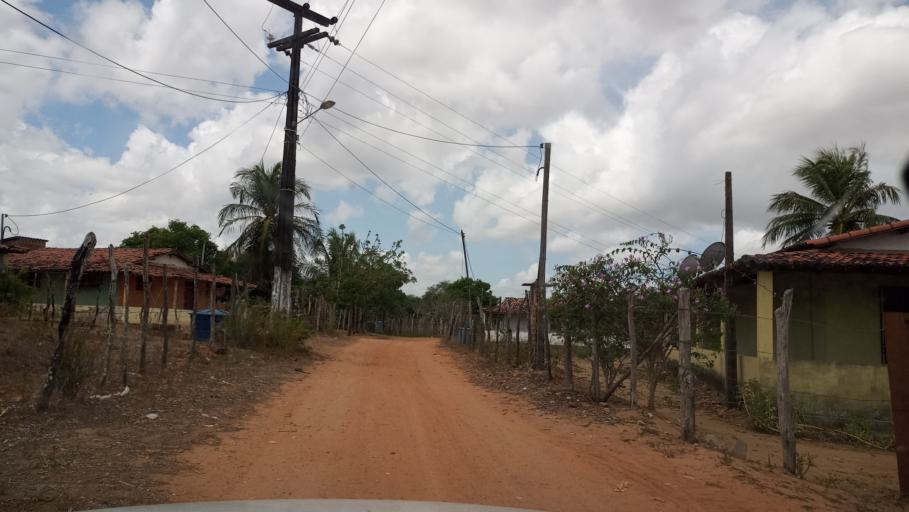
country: BR
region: Rio Grande do Norte
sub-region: Goianinha
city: Goianinha
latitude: -6.3033
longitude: -35.2739
